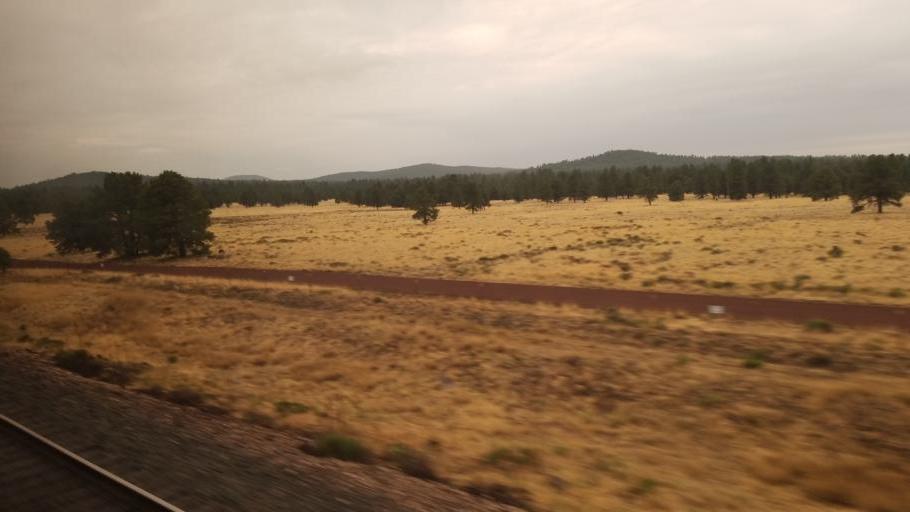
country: US
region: Arizona
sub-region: Coconino County
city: Parks
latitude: 35.2244
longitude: -111.8026
